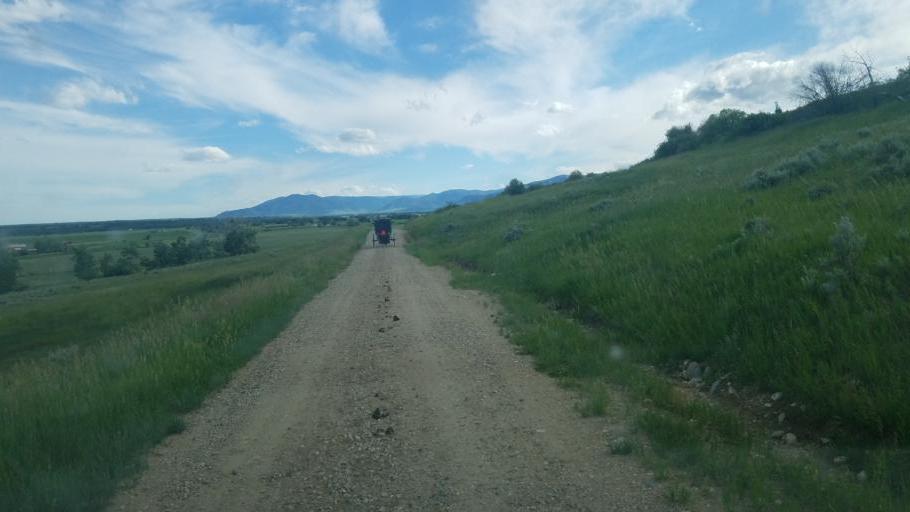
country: US
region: Montana
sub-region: Carbon County
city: Red Lodge
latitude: 45.3665
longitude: -109.1907
